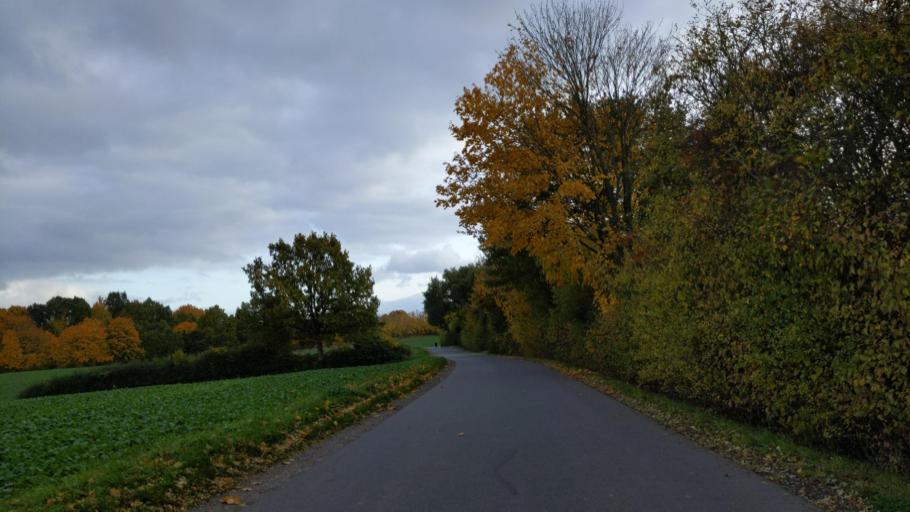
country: DE
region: Schleswig-Holstein
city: Sierksdorf
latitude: 54.0968
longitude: 10.7728
